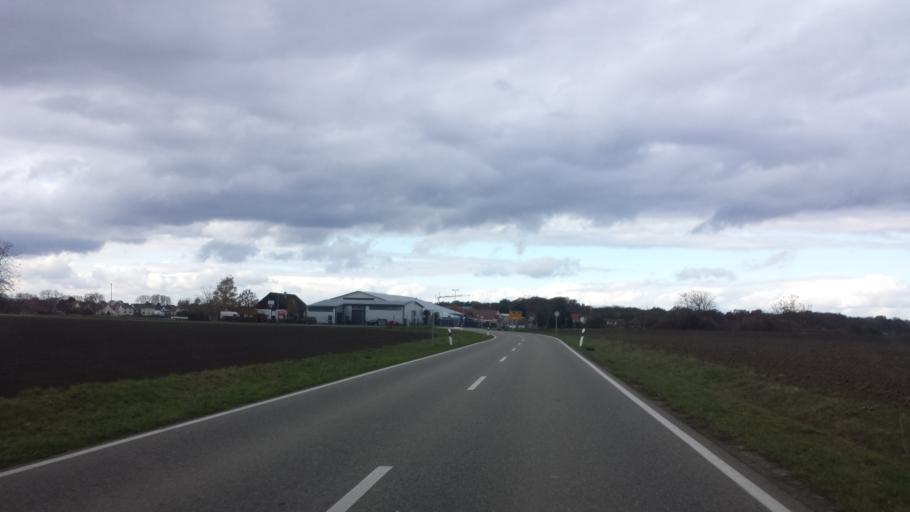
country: DE
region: Rheinland-Pfalz
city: Waldsee
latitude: 49.4006
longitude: 8.4472
